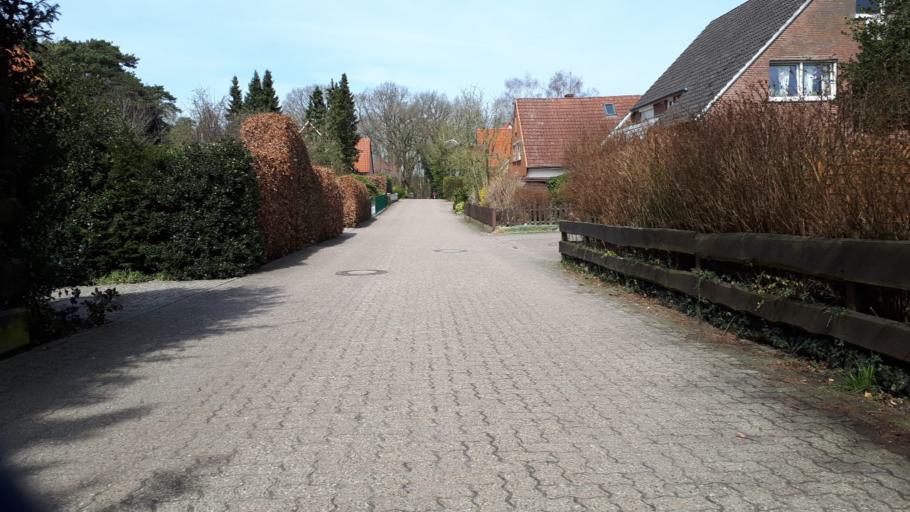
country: DE
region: Lower Saxony
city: Wardenburg
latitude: 53.0759
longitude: 8.2038
